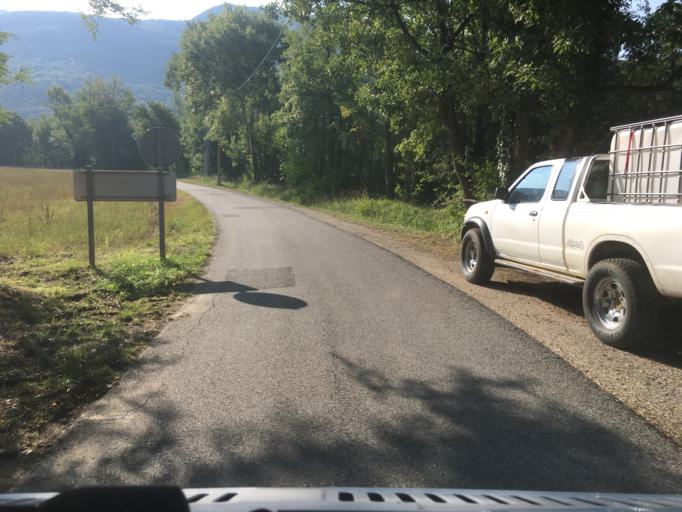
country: FR
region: Provence-Alpes-Cote d'Azur
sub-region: Departement des Alpes-de-Haute-Provence
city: Mallemoisson
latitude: 43.9396
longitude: 6.1899
